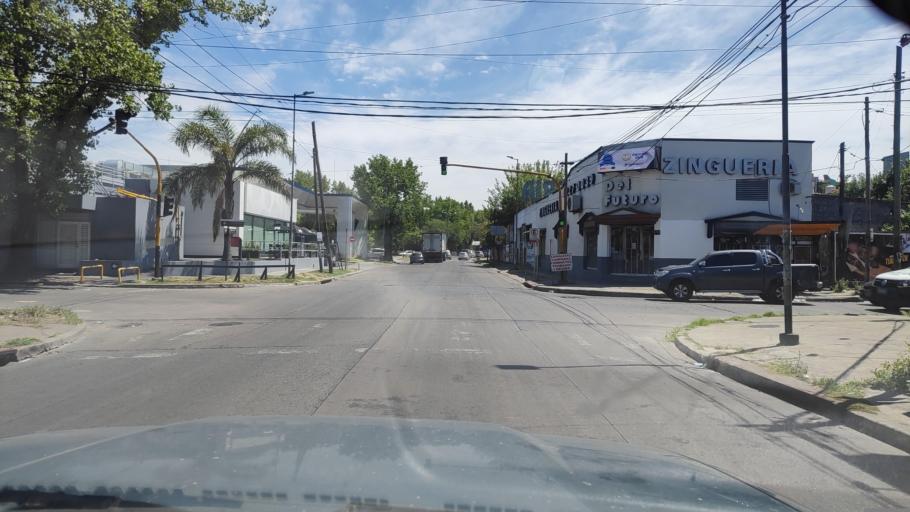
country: AR
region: Buenos Aires
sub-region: Partido de Moron
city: Moron
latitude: -34.6538
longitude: -58.6299
